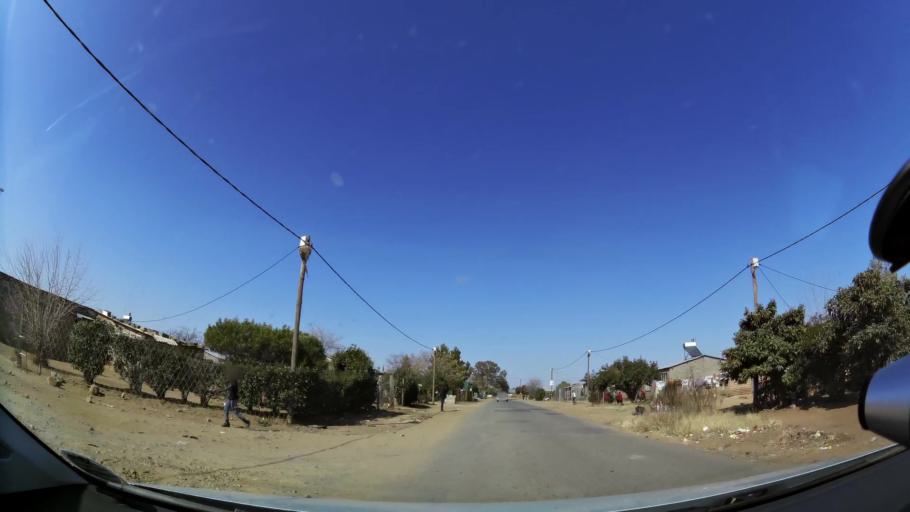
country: ZA
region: Orange Free State
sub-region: Mangaung Metropolitan Municipality
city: Bloemfontein
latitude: -29.1544
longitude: 26.2501
